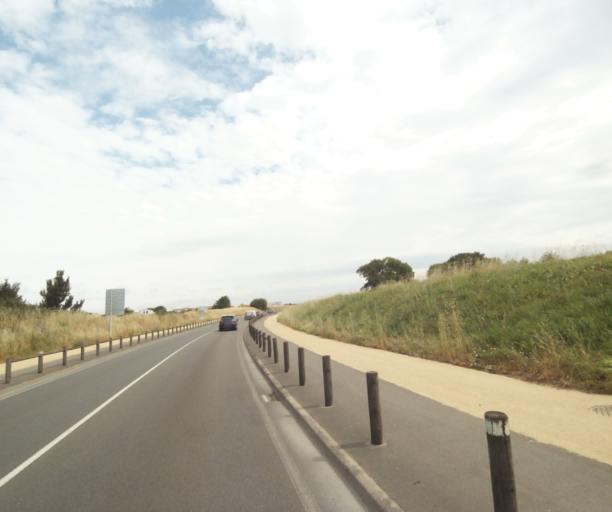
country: FR
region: Pays de la Loire
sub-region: Departement de la Vendee
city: Chateau-d'Olonne
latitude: 46.5030
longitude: -1.7592
